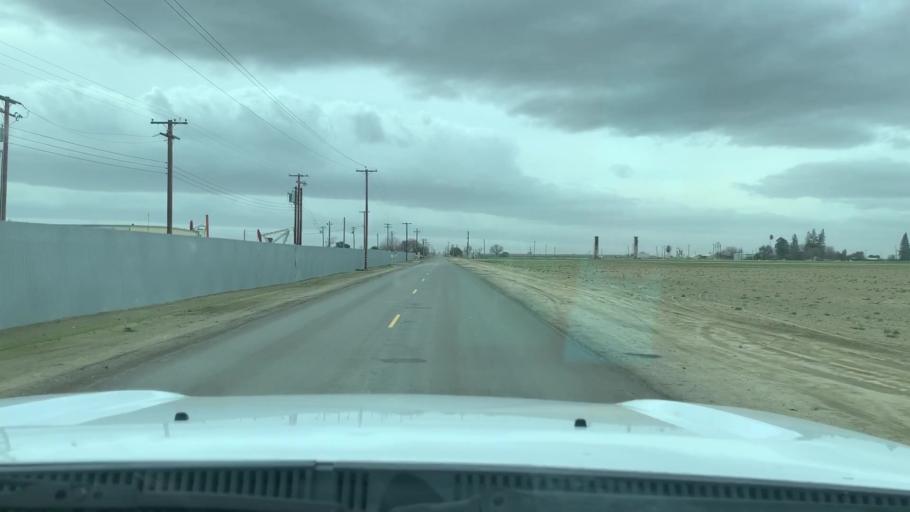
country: US
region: California
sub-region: Kern County
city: Shafter
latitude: 35.5292
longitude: -119.2703
